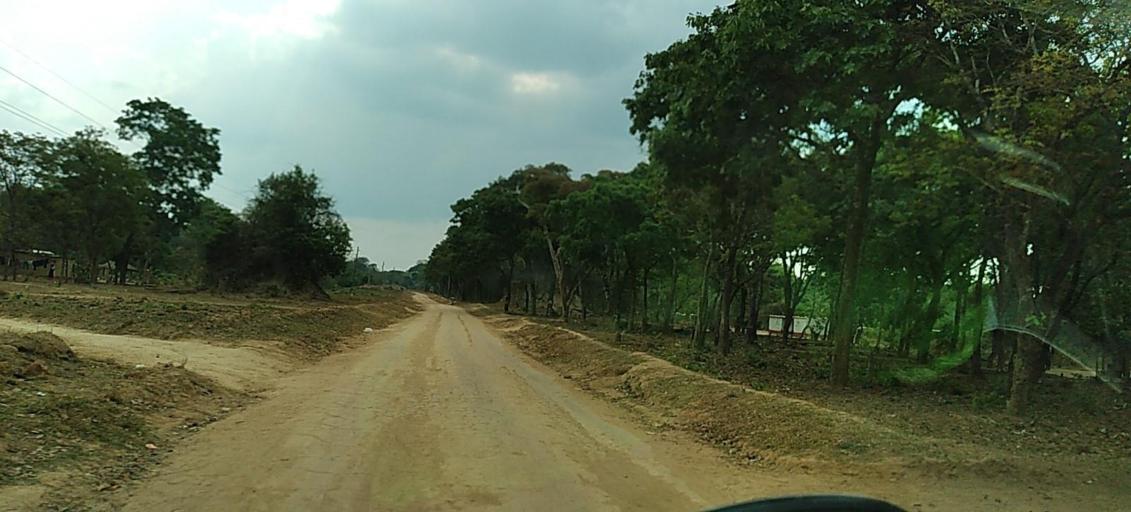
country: ZM
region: North-Western
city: Solwezi
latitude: -12.7849
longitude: 26.5100
